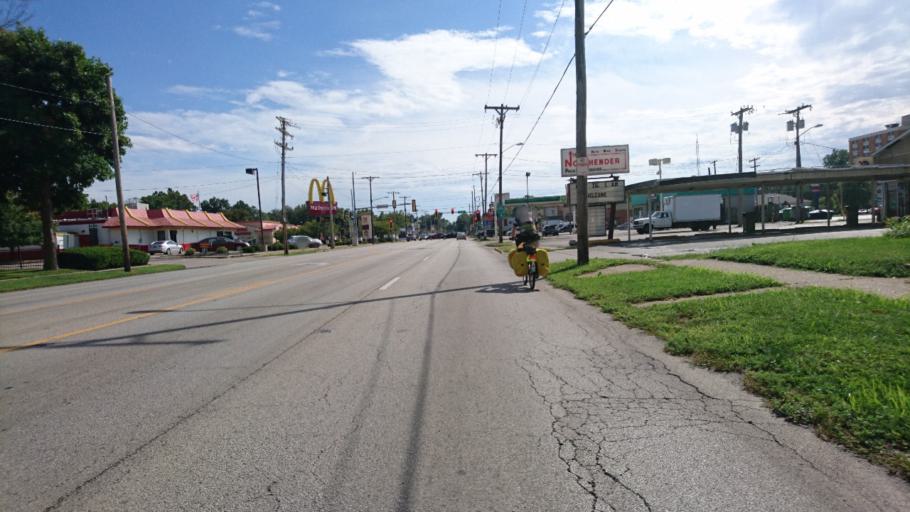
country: US
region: Illinois
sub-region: Sangamon County
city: Springfield
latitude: 39.8175
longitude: -89.6433
